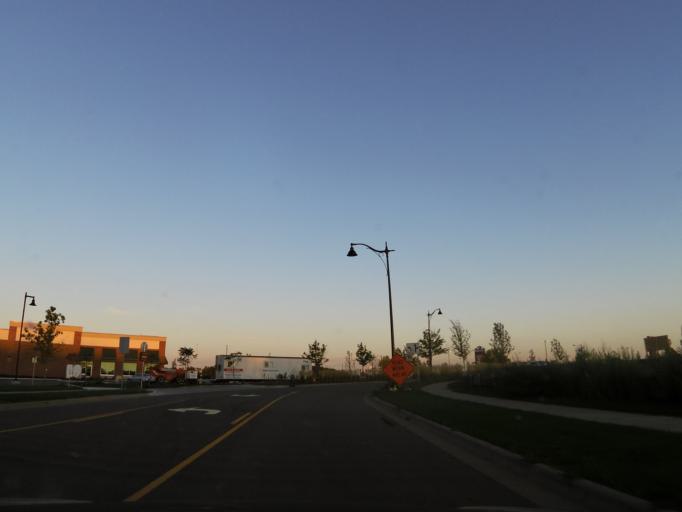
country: US
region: Minnesota
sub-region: Washington County
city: Oakdale
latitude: 44.9647
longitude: -92.9626
